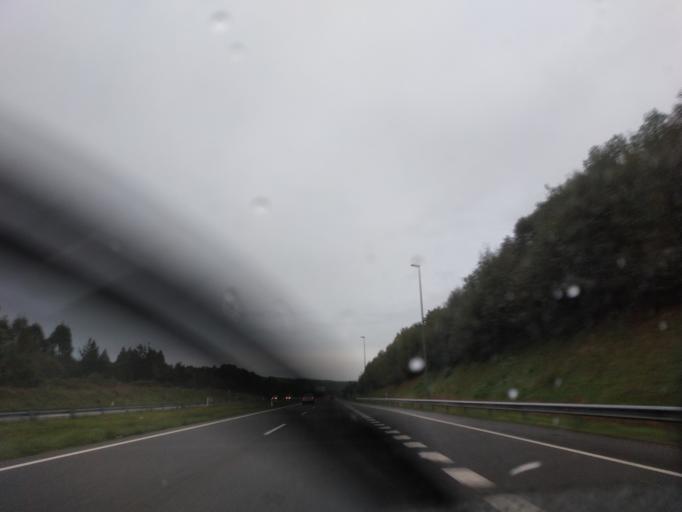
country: ES
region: Galicia
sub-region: Provincia de Lugo
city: Begonte
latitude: 43.1765
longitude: -7.7323
